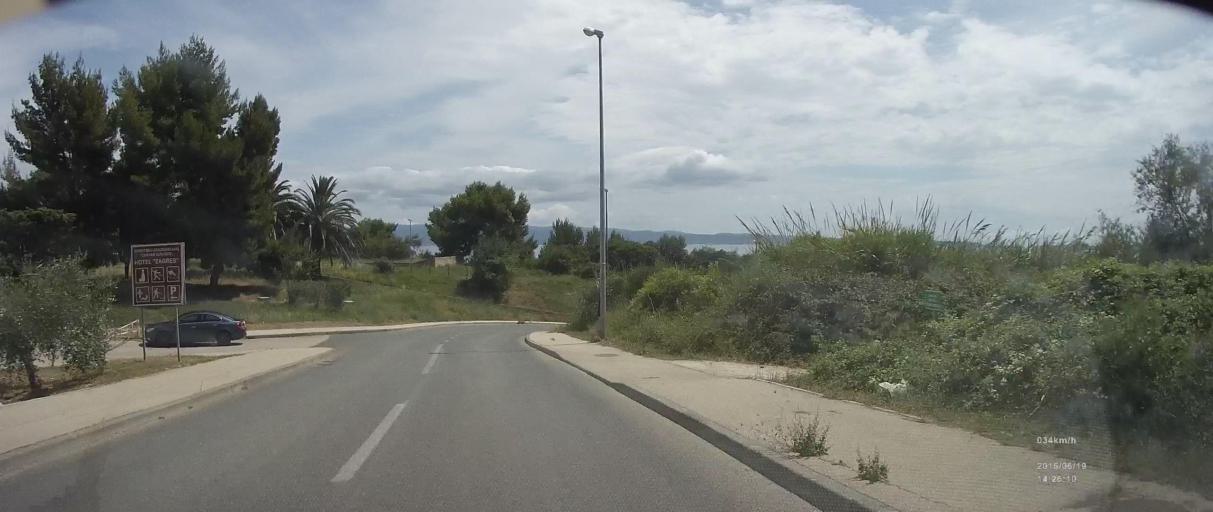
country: HR
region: Splitsko-Dalmatinska
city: Kamen
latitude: 43.5028
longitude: 16.4925
